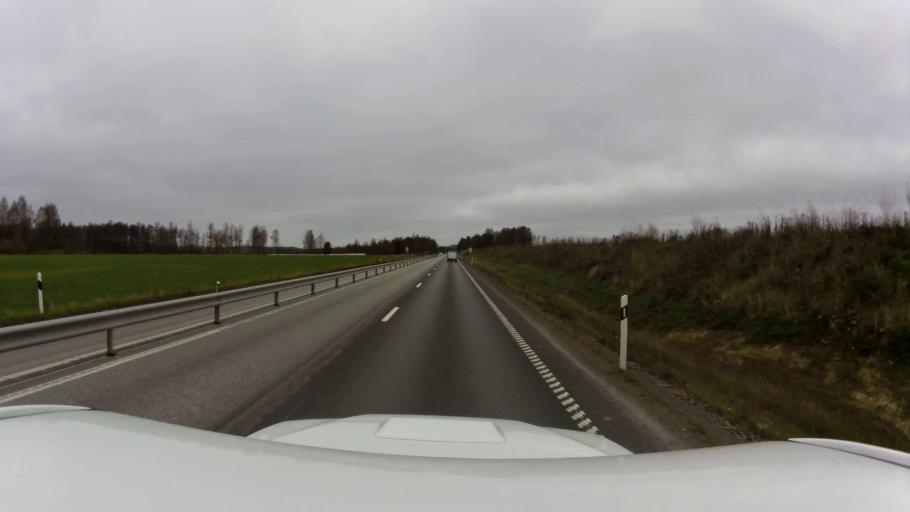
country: SE
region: OEstergoetland
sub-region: Kinda Kommun
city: Rimforsa
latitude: 58.1455
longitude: 15.6808
